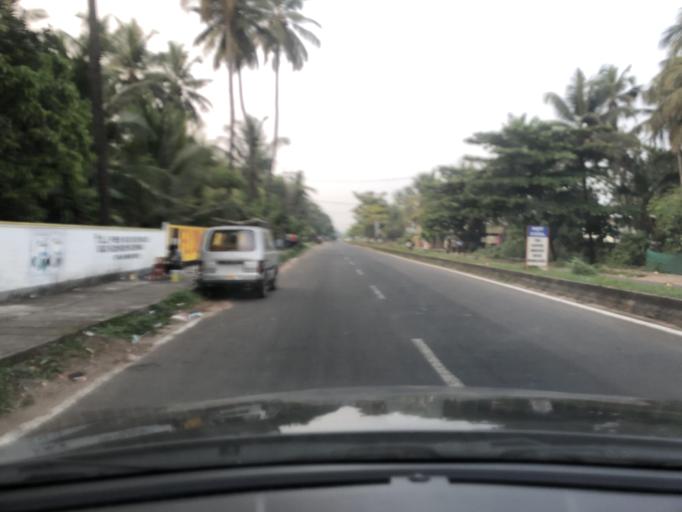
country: IN
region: Kerala
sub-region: Kozhikode
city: Kozhikode
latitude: 11.2920
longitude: 75.7582
